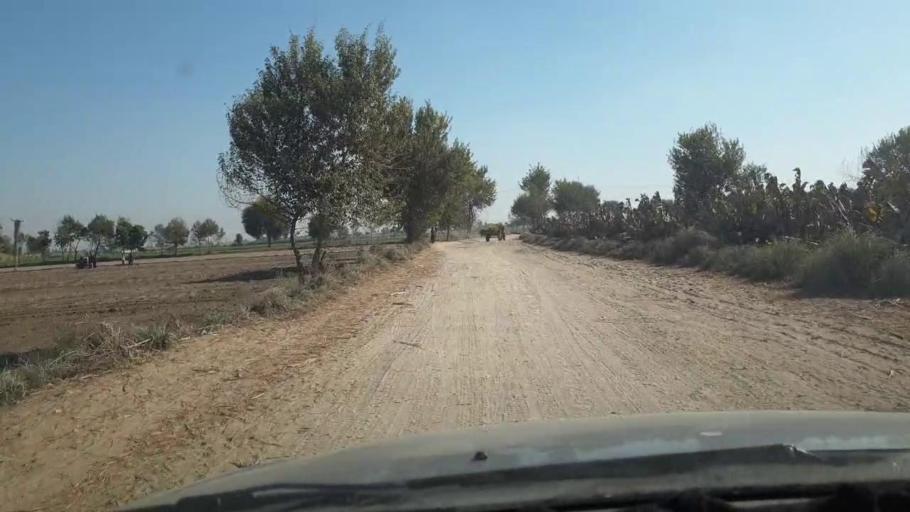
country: PK
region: Sindh
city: Ghotki
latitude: 28.0229
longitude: 69.2211
